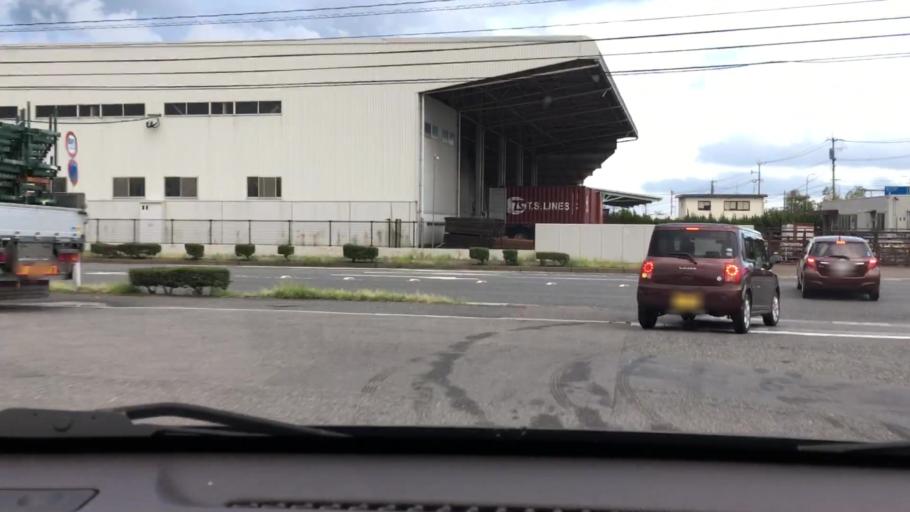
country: JP
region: Yamaguchi
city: Shimonoseki
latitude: 33.8876
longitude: 130.9879
